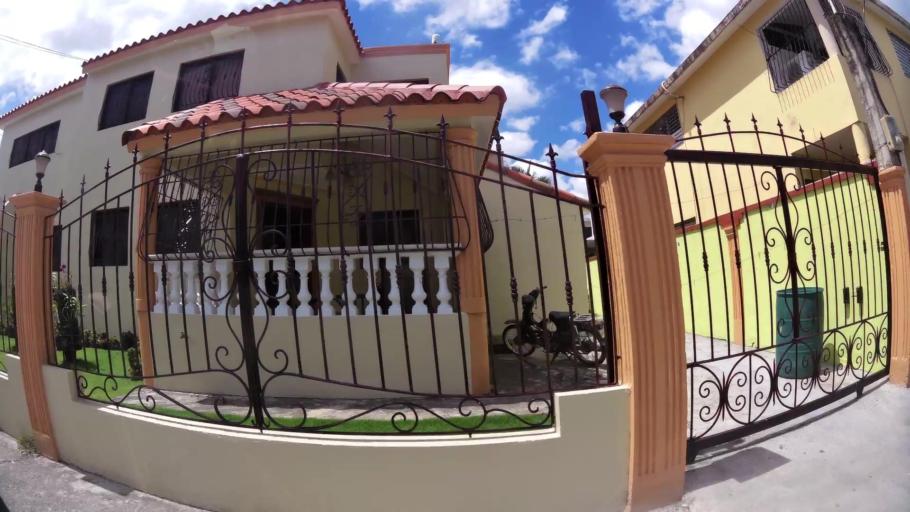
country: DO
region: San Cristobal
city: San Cristobal
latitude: 18.4111
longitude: -70.1030
